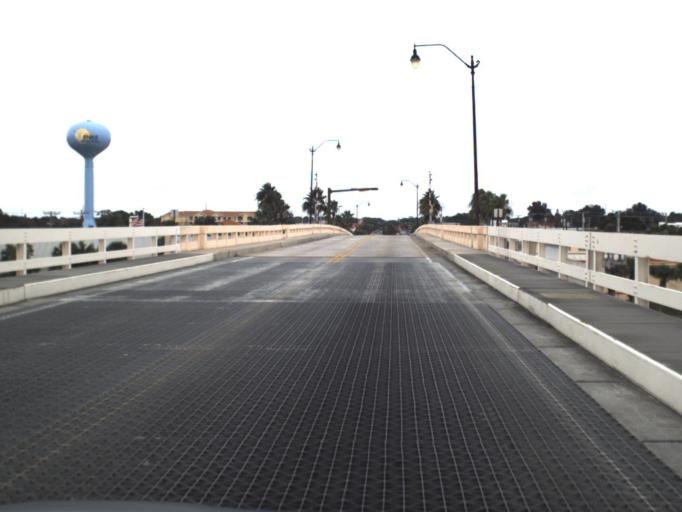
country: US
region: Florida
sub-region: Sarasota County
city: Venice
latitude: 27.0998
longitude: -82.4410
